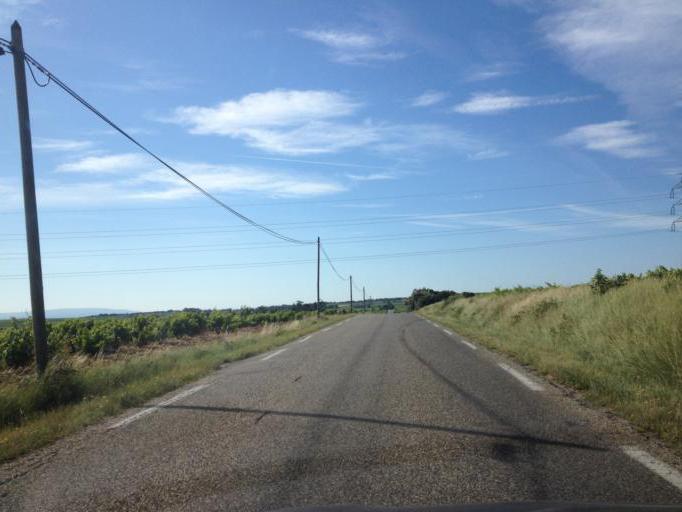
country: FR
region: Provence-Alpes-Cote d'Azur
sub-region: Departement du Vaucluse
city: Orange
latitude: 44.1005
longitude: 4.8232
